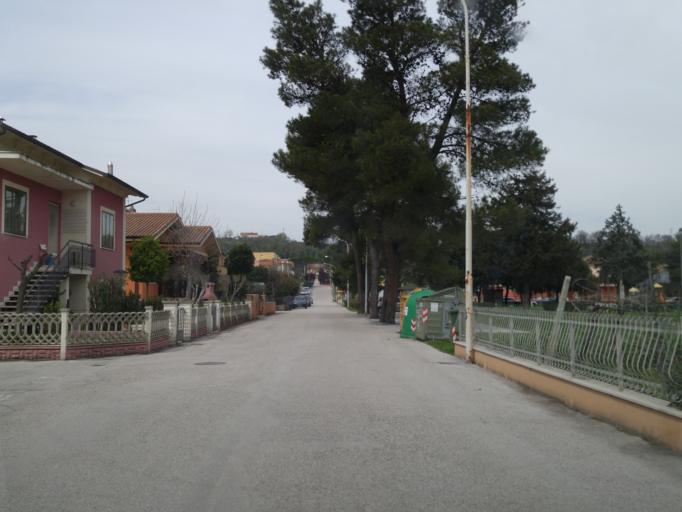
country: IT
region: The Marches
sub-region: Provincia di Pesaro e Urbino
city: Tavernelle
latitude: 43.7352
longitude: 12.8991
